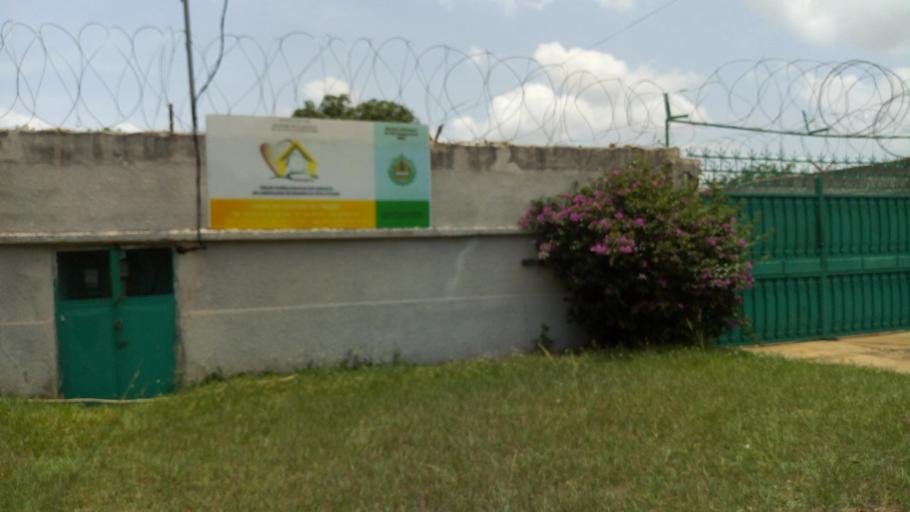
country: CI
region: Vallee du Bandama
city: Bouake
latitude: 7.6860
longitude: -4.9993
